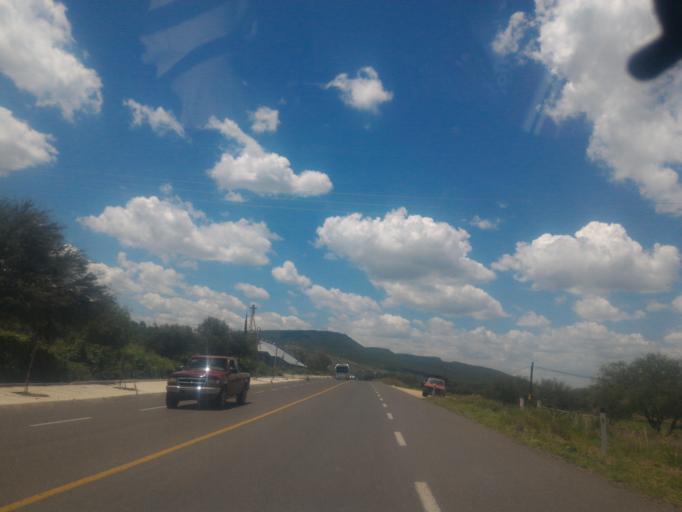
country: MX
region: Guanajuato
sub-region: San Francisco del Rincon
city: San Ignacio de Hidalgo
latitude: 20.9121
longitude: -101.9170
